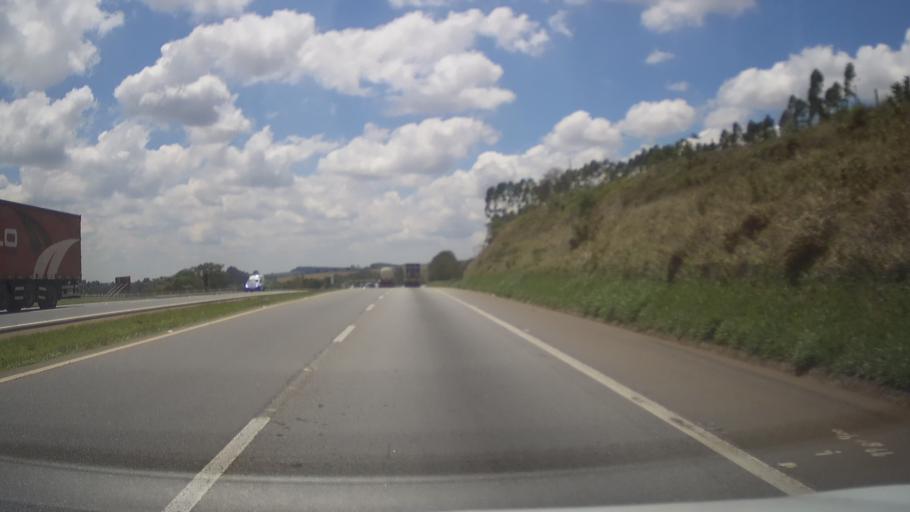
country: BR
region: Minas Gerais
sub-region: Campanha
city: Campanha
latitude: -21.7998
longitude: -45.4655
